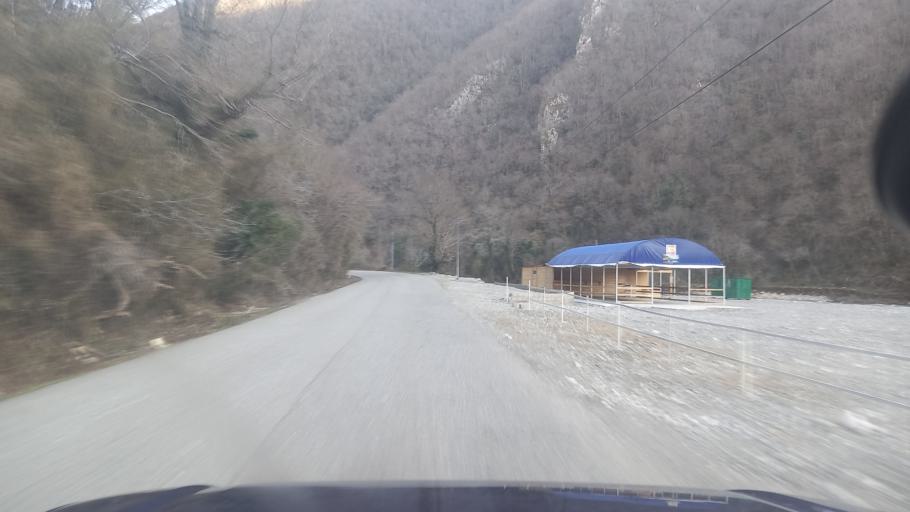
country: GE
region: Abkhazia
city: Bich'vinta
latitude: 43.2511
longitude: 40.3992
